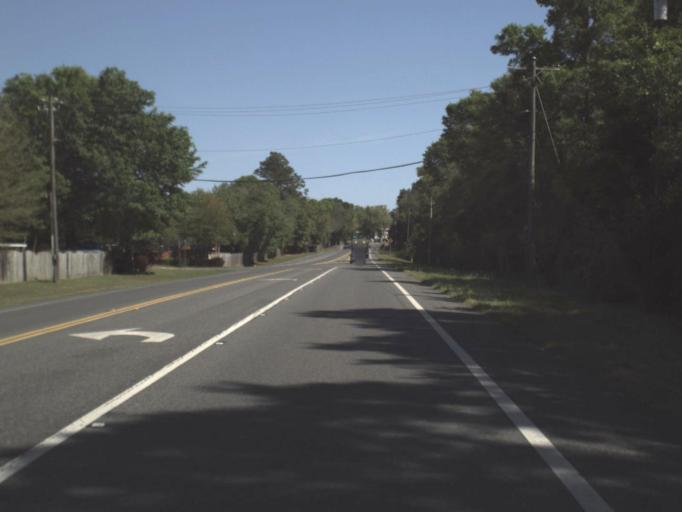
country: US
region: Florida
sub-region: Escambia County
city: Bellview
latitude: 30.4900
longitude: -87.3202
